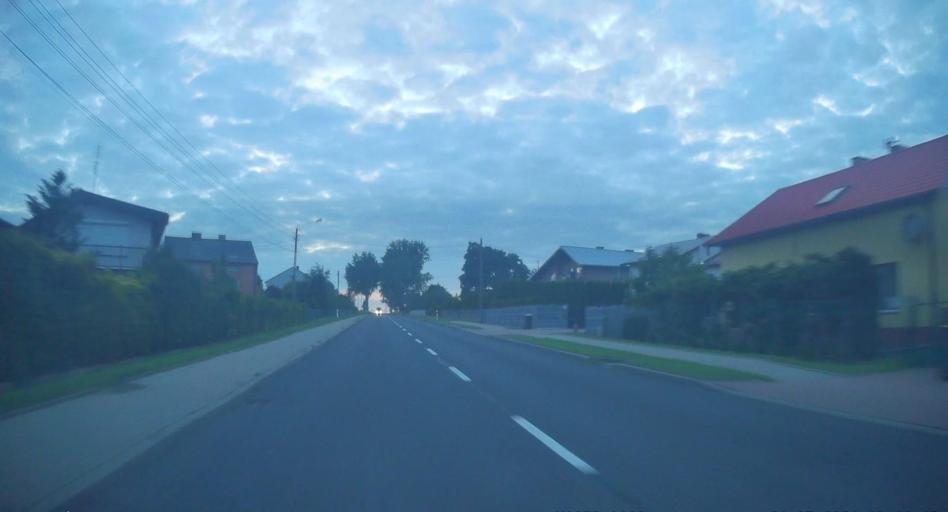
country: PL
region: Opole Voivodeship
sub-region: Powiat oleski
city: Dalachow
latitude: 51.0271
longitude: 18.6396
